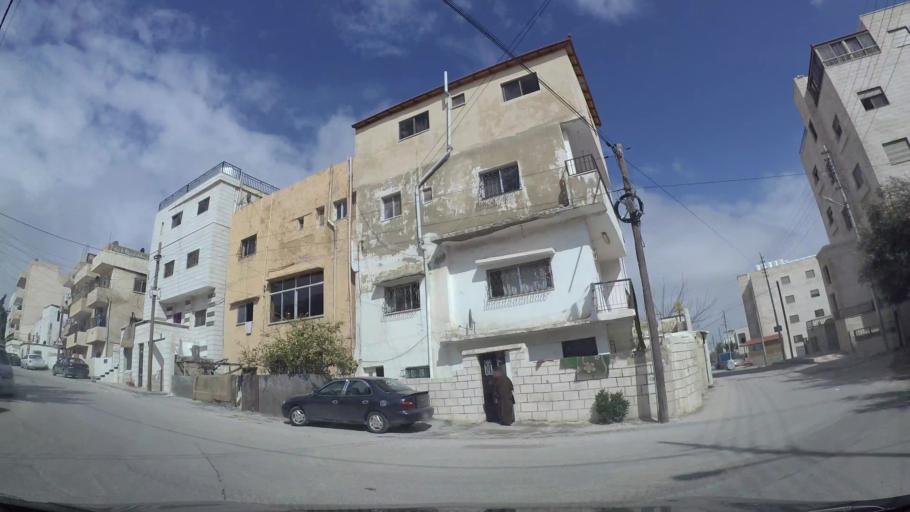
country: JO
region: Amman
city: Wadi as Sir
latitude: 31.9502
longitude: 35.8297
